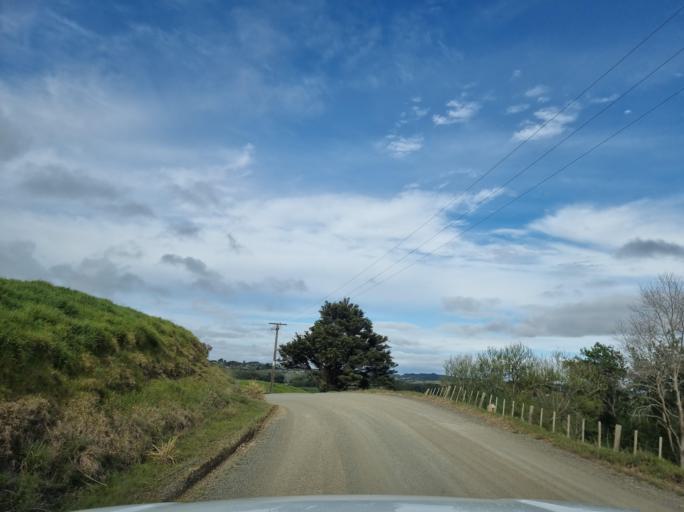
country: NZ
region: Northland
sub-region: Whangarei
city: Ruakaka
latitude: -36.0928
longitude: 174.3662
